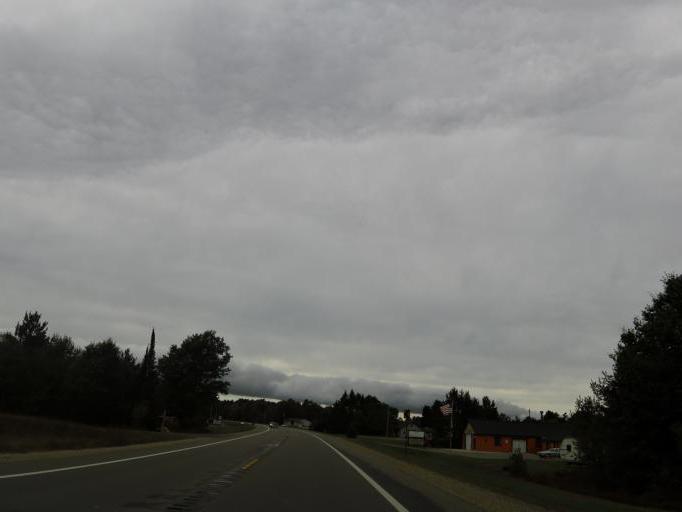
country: US
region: Michigan
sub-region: Roscommon County
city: Roscommon
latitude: 44.5089
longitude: -84.6100
